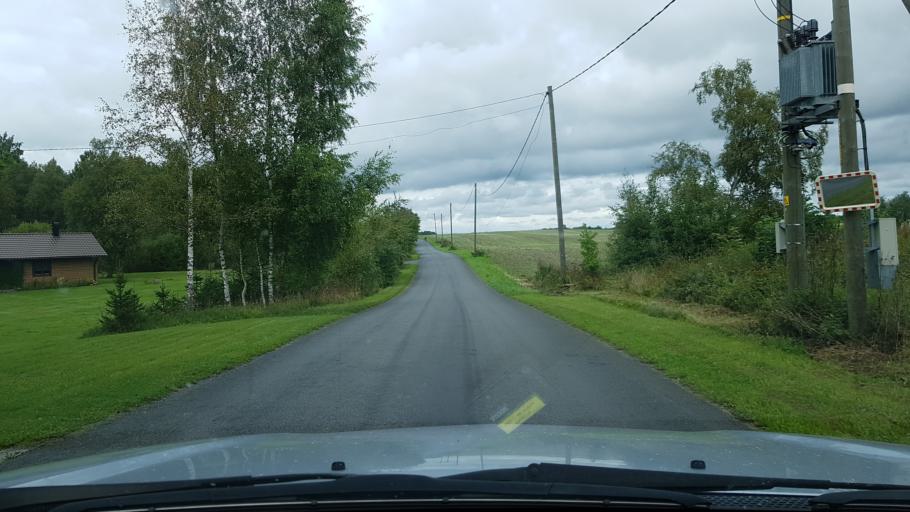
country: EE
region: Harju
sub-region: Rae vald
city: Vaida
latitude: 59.3494
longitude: 24.9627
